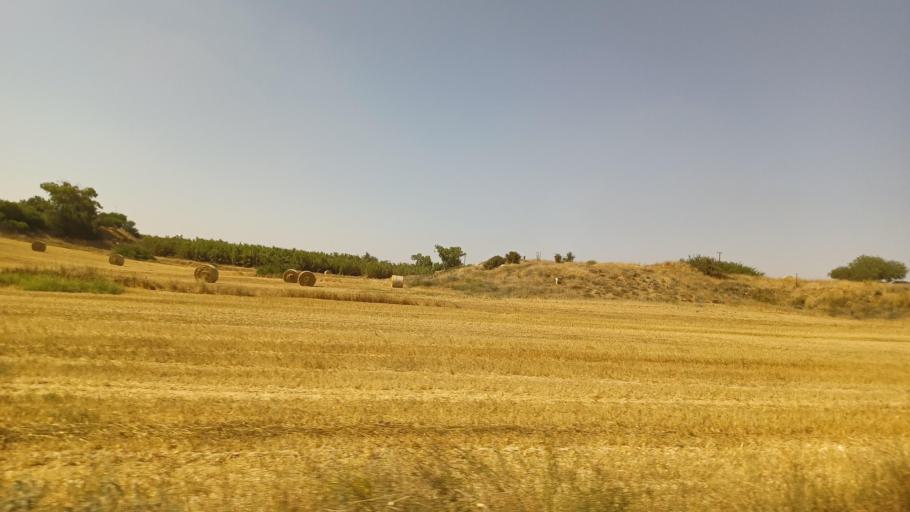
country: CY
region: Ammochostos
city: Acheritou
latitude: 35.0723
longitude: 33.8696
